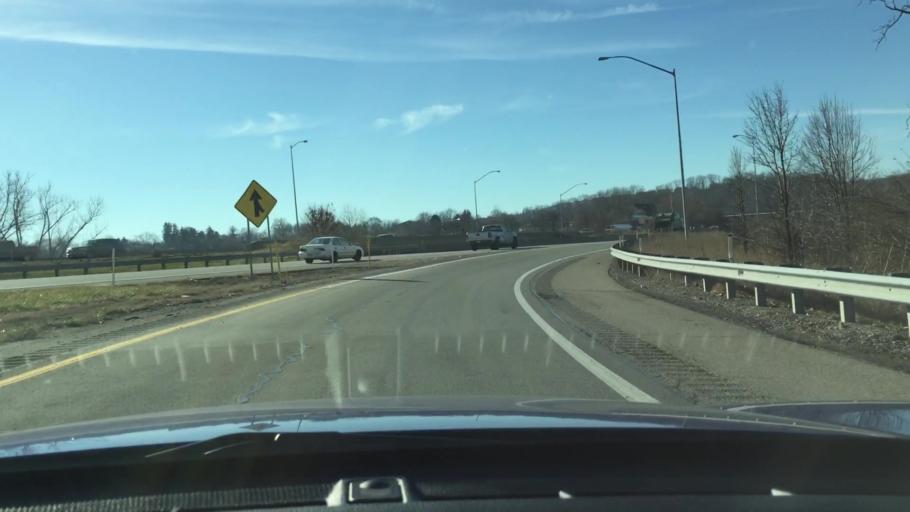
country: US
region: Pennsylvania
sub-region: Allegheny County
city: Bridgeville
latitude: 40.3731
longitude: -80.1076
